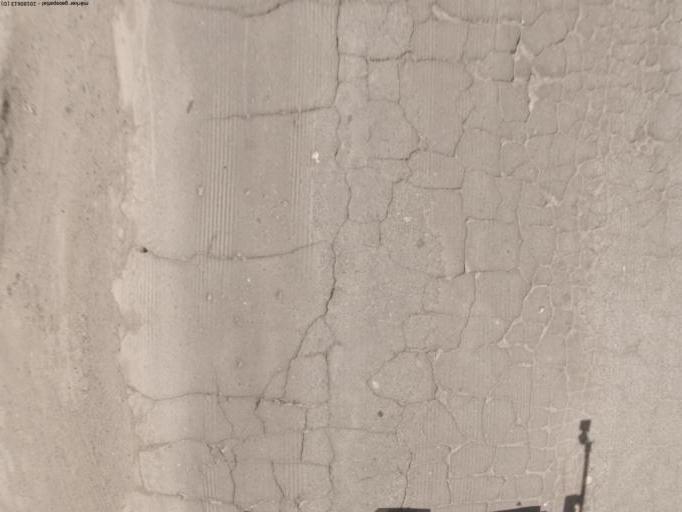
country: US
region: California
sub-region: Madera County
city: Chowchilla
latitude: 37.0737
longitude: -120.4372
